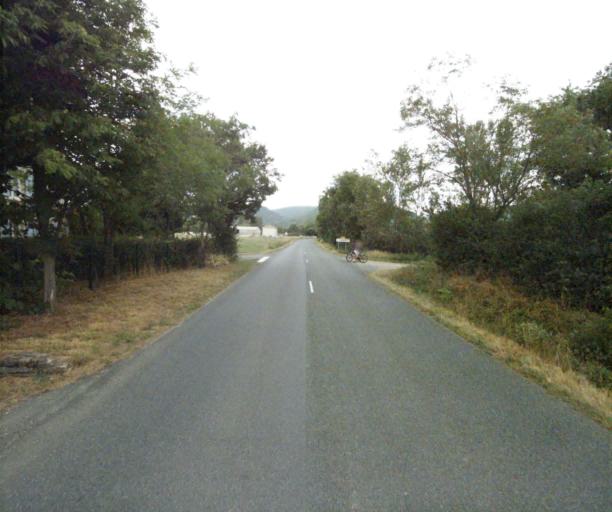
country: FR
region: Midi-Pyrenees
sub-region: Departement du Tarn
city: Soreze
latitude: 43.4571
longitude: 2.0478
